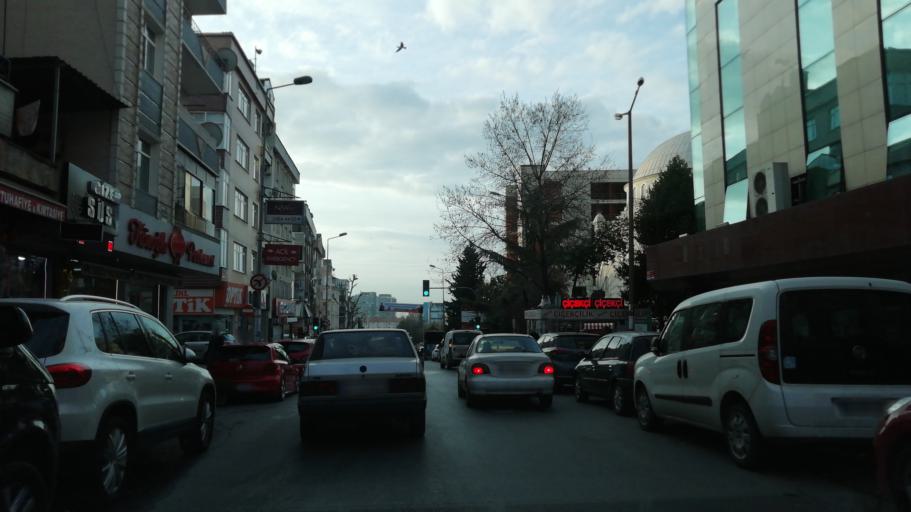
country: TR
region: Istanbul
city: Bahcelievler
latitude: 40.9995
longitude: 28.8305
